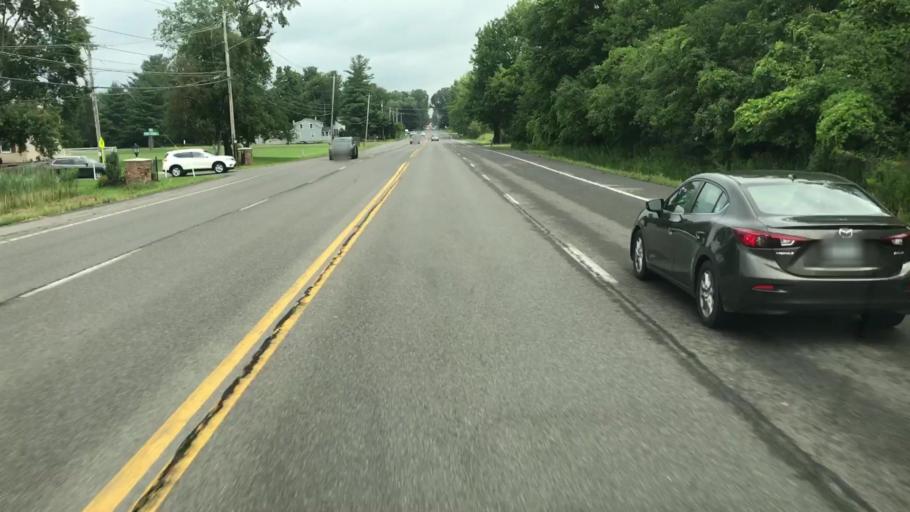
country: US
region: New York
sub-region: Onondaga County
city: Liverpool
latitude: 43.1460
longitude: -76.2072
